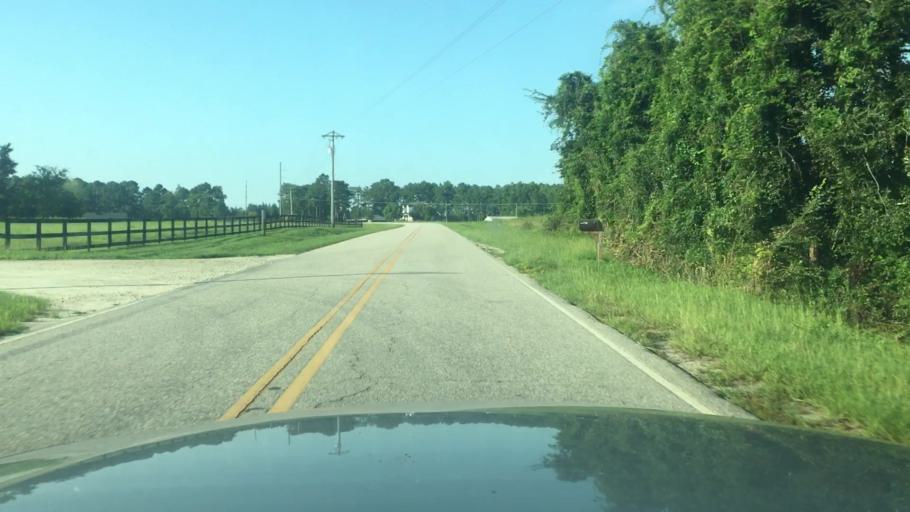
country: US
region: North Carolina
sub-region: Cumberland County
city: Spring Lake
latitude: 35.2148
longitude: -78.8948
